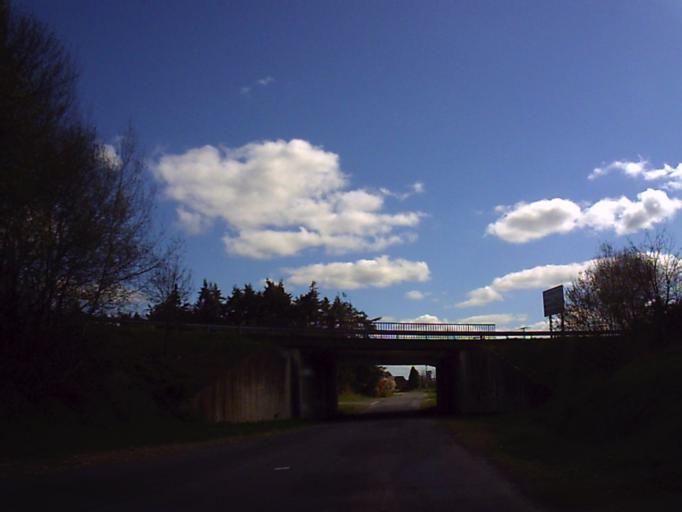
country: FR
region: Brittany
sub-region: Departement d'Ille-et-Vilaine
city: Saint-Meen-le-Grand
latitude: 48.1823
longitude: -2.1844
